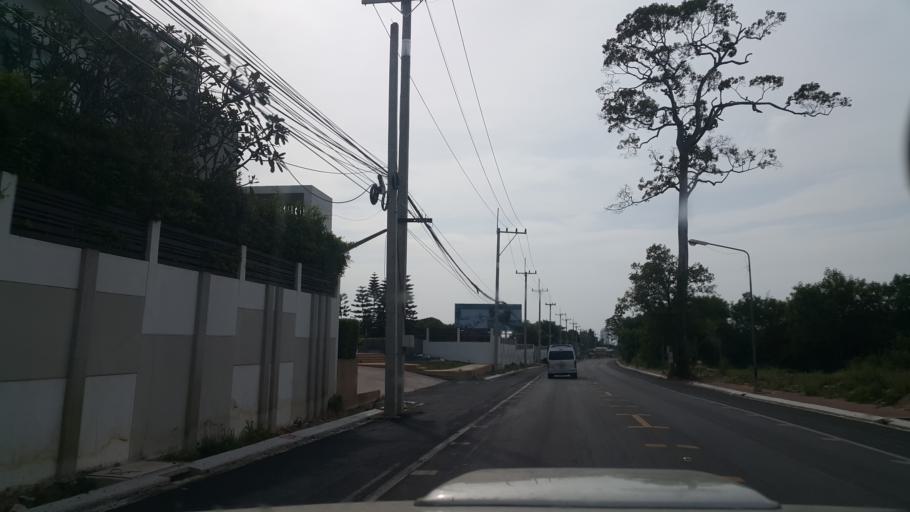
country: TH
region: Chon Buri
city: Sattahip
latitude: 12.7781
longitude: 100.9431
